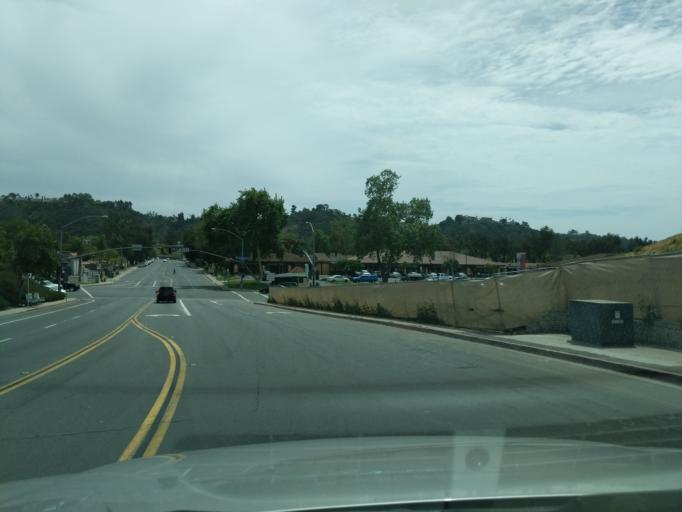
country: US
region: California
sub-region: San Diego County
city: San Diego
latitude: 32.7858
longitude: -117.1104
